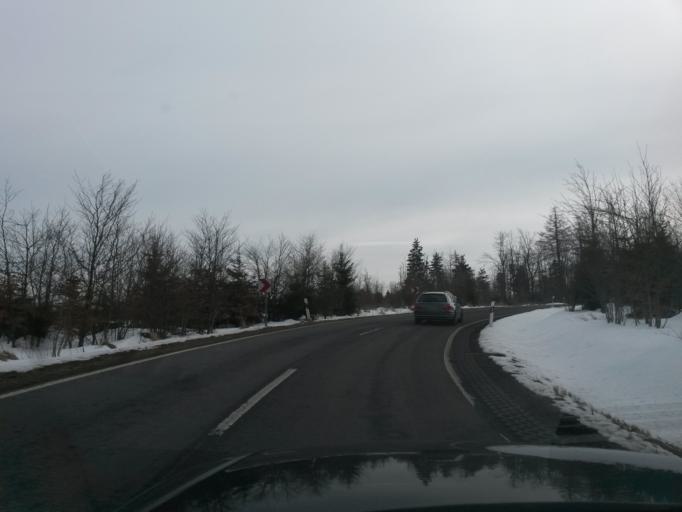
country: DE
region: Thuringia
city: Birx
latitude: 50.5505
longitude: 10.0484
